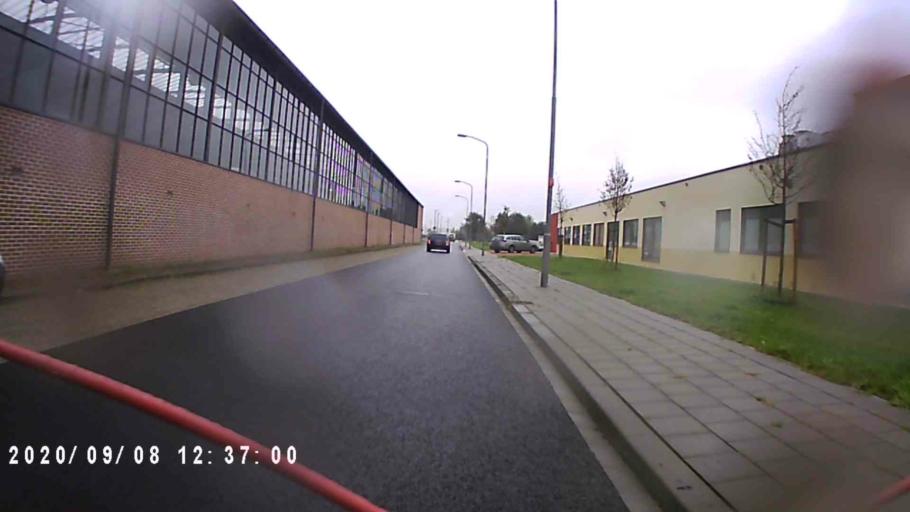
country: NL
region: Groningen
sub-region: Gemeente Veendam
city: Veendam
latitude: 53.1026
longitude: 6.8835
